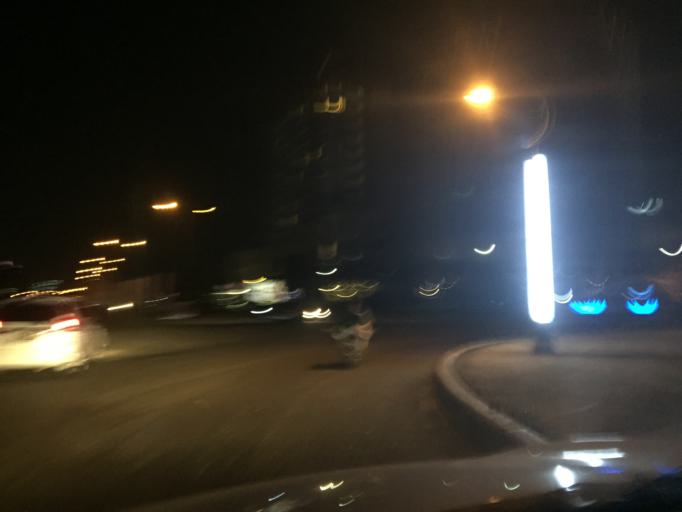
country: ID
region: Banten
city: Tangerang
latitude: -6.2435
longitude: 106.6290
